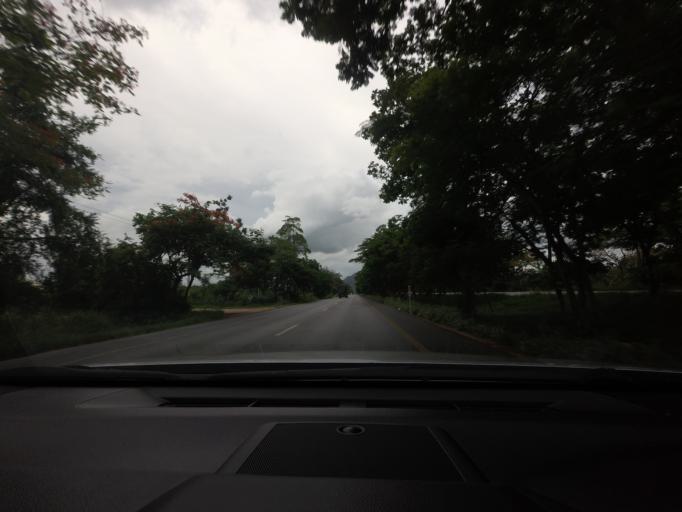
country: TH
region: Phetchaburi
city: Cha-am
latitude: 12.7811
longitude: 99.9377
